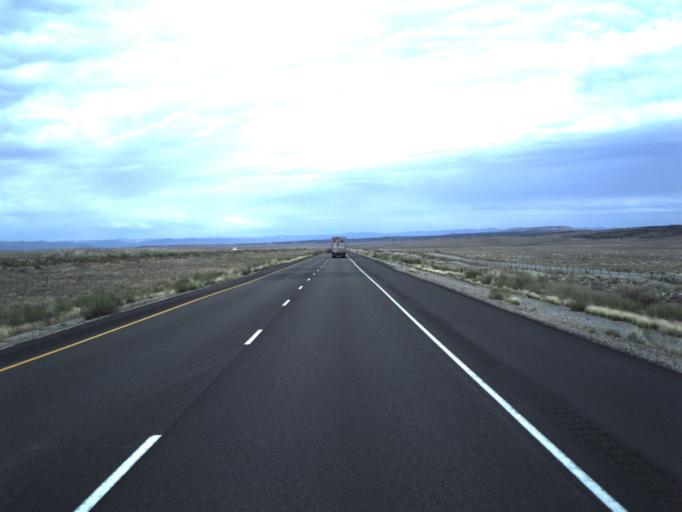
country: US
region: Colorado
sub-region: Mesa County
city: Loma
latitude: 39.0540
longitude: -109.2615
